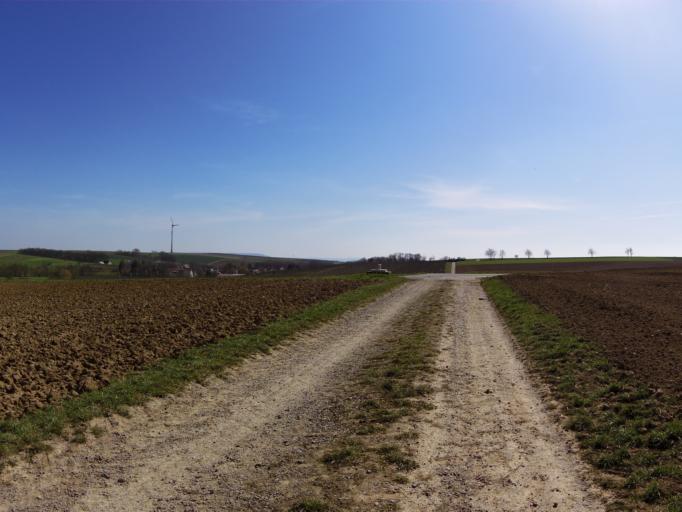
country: DE
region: Bavaria
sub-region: Regierungsbezirk Unterfranken
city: Prosselsheim
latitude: 49.8466
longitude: 10.1389
